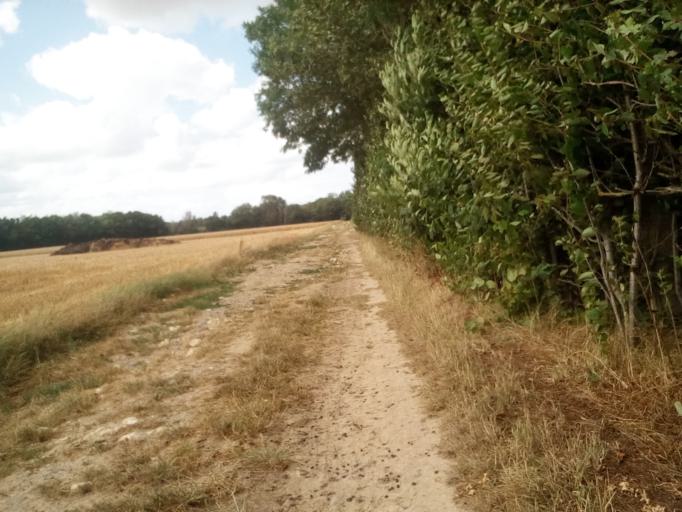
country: FR
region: Lower Normandy
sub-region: Departement du Calvados
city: Creully
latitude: 49.3009
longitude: -0.5703
